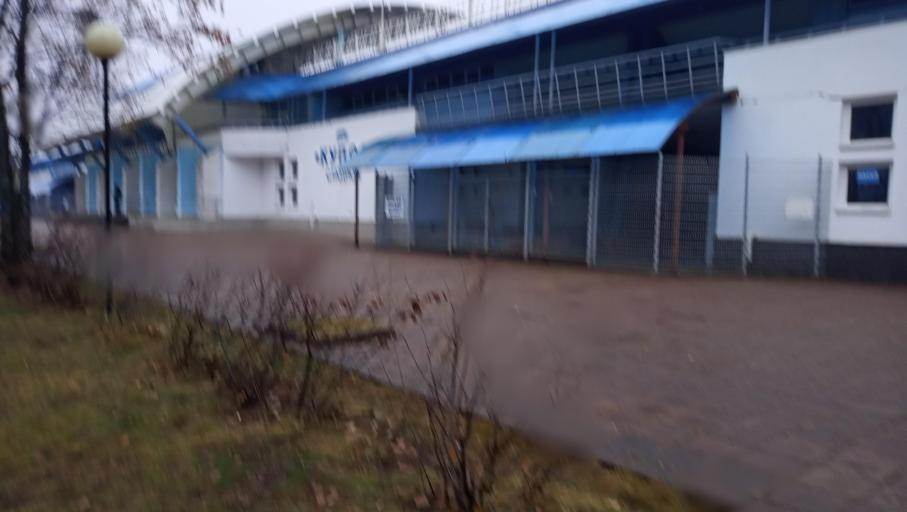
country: RU
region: Udmurtiya
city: Izhevsk
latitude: 56.8610
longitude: 53.1708
